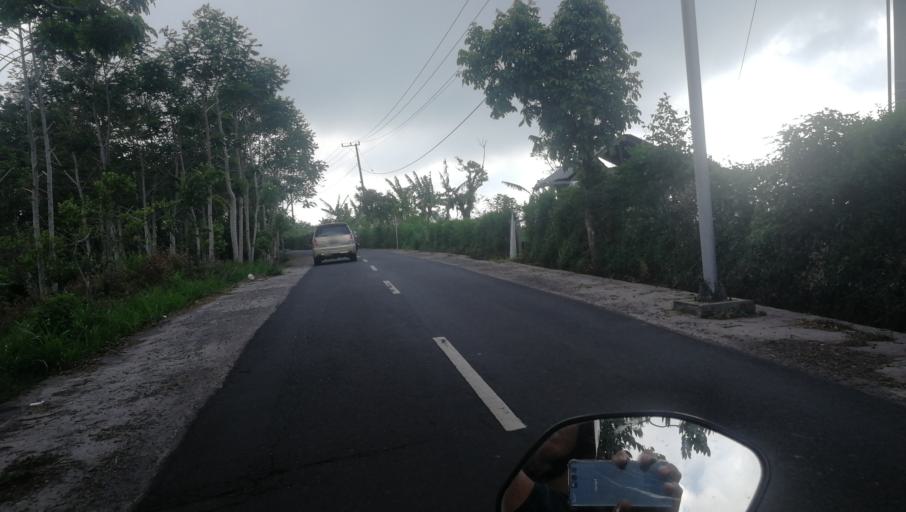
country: ID
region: Bali
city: Munduk
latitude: -8.2511
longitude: 115.0936
